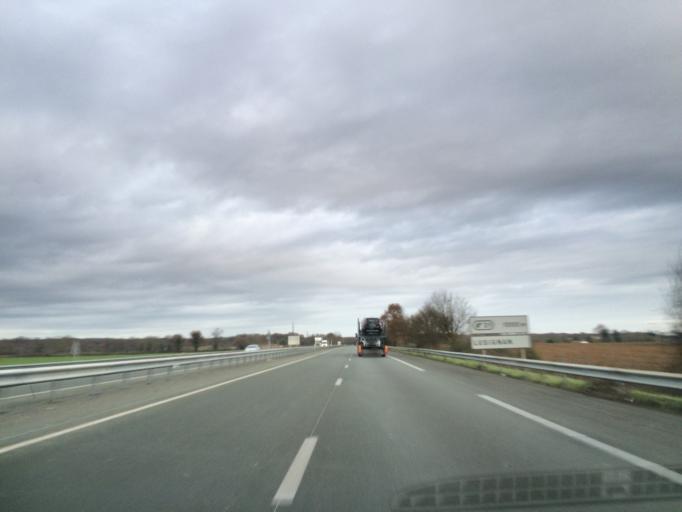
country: FR
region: Poitou-Charentes
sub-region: Departement des Deux-Sevres
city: Pamproux
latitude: 46.4223
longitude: -0.0976
